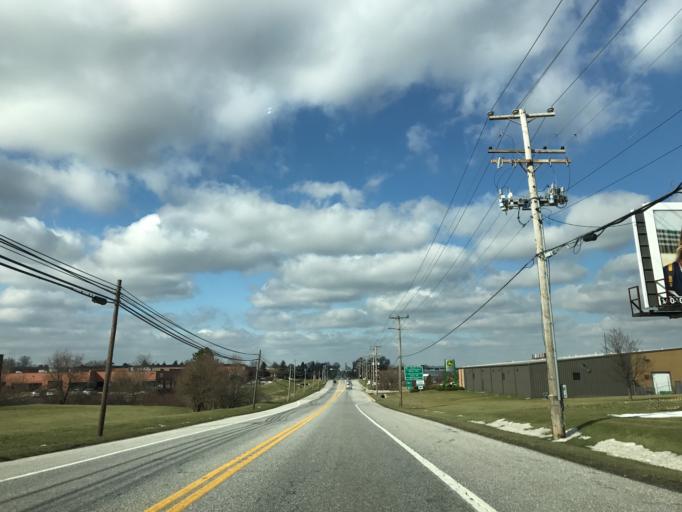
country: US
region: Maryland
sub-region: Carroll County
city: Westminster
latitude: 39.6031
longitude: -76.9985
